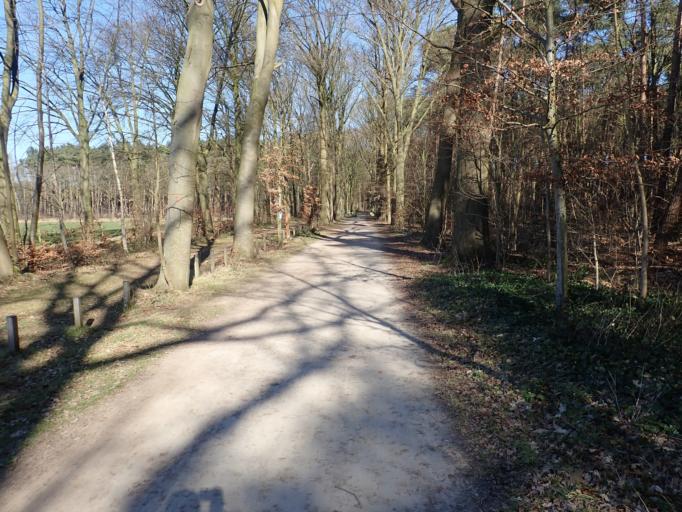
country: BE
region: Flanders
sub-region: Provincie Antwerpen
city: Zoersel
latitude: 51.2867
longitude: 4.6601
